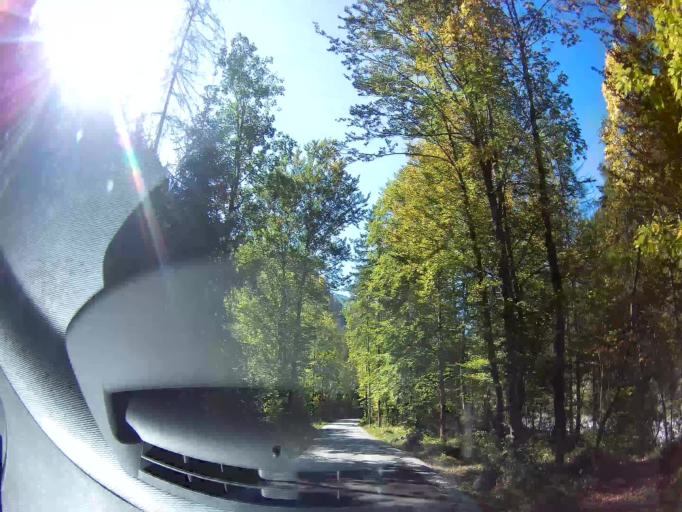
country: AT
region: Salzburg
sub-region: Politischer Bezirk Zell am See
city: Sankt Martin bei Lofer
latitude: 47.5255
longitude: 12.7134
